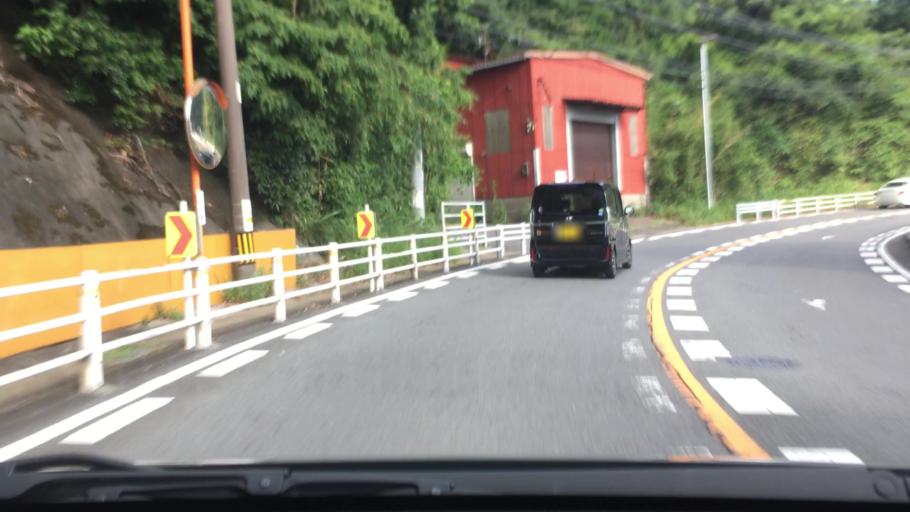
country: JP
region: Nagasaki
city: Togitsu
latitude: 32.8112
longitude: 129.8103
